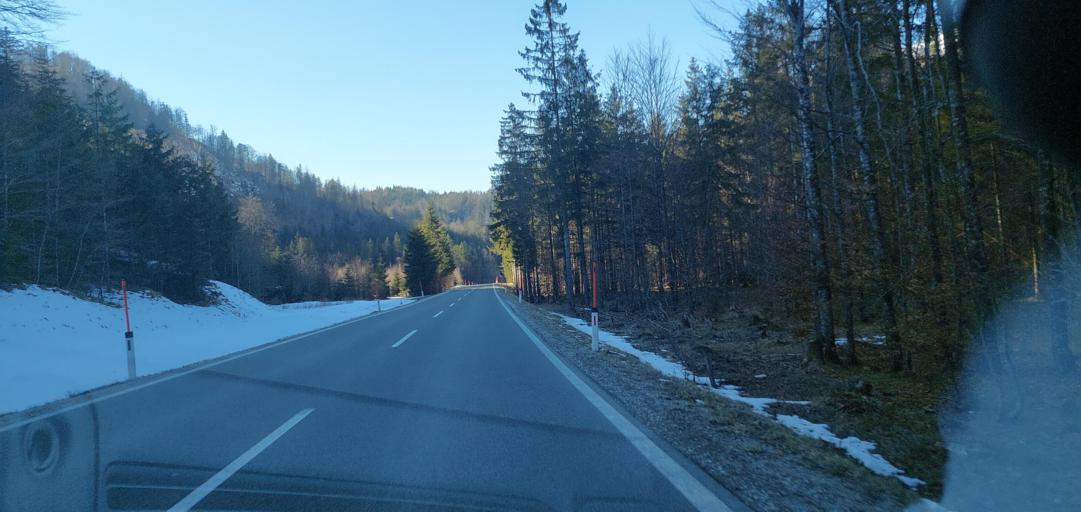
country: AT
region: Upper Austria
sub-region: Politischer Bezirk Gmunden
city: Bad Ischl
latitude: 47.7775
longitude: 13.5992
